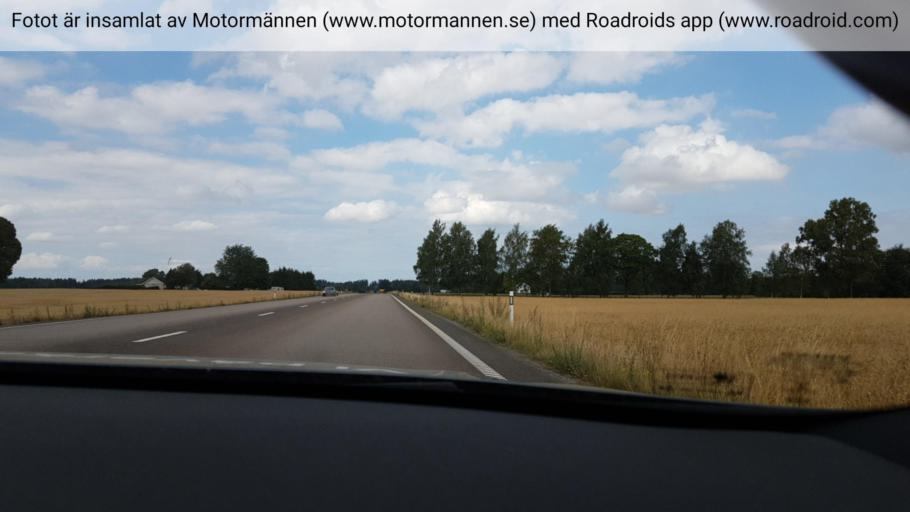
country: SE
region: Vaestra Goetaland
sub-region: Skara Kommun
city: Skara
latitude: 58.4056
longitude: 13.3897
